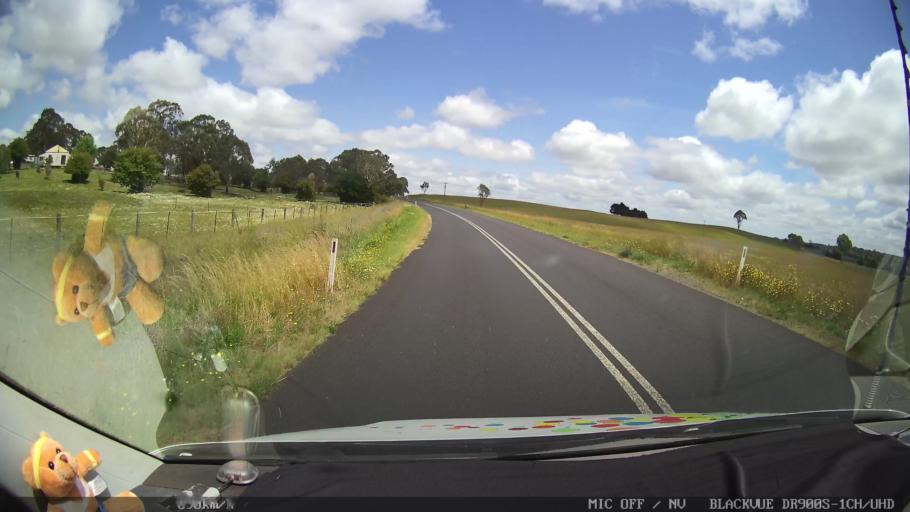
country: AU
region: New South Wales
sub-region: Glen Innes Severn
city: Glen Innes
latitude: -29.6990
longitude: 151.7182
